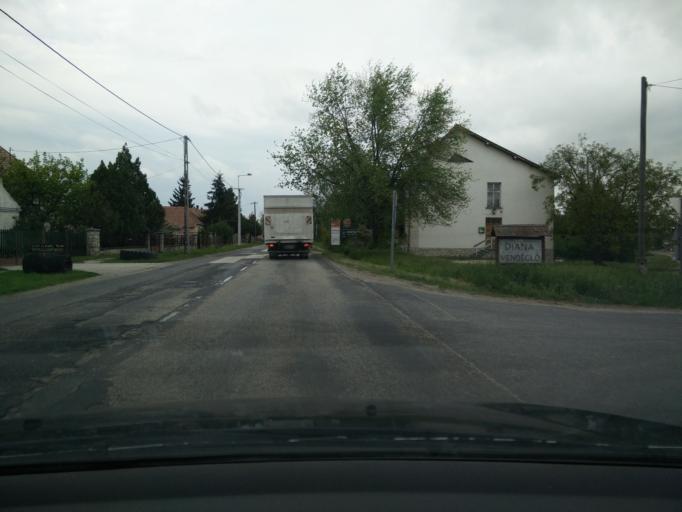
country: HU
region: Gyor-Moson-Sopron
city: Gyorszemere
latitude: 47.5491
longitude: 17.5579
